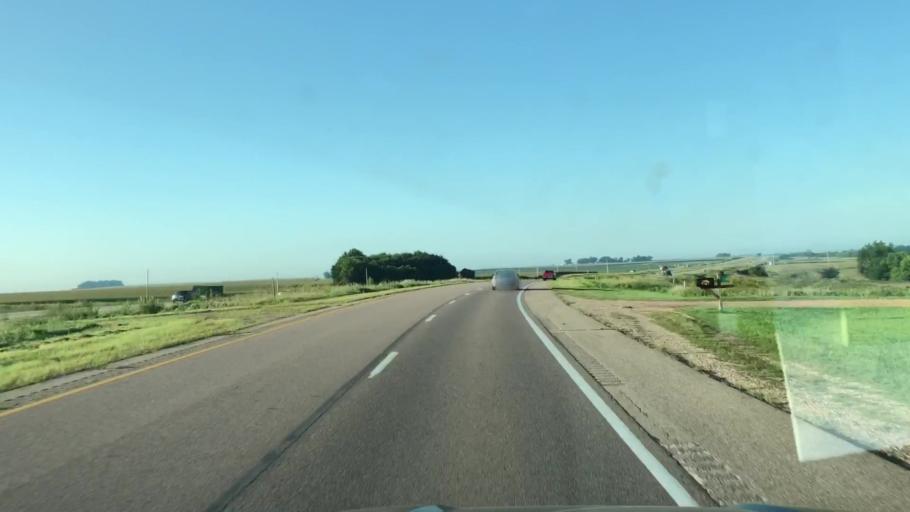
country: US
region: Iowa
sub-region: O'Brien County
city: Sheldon
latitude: 43.1334
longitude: -95.8811
